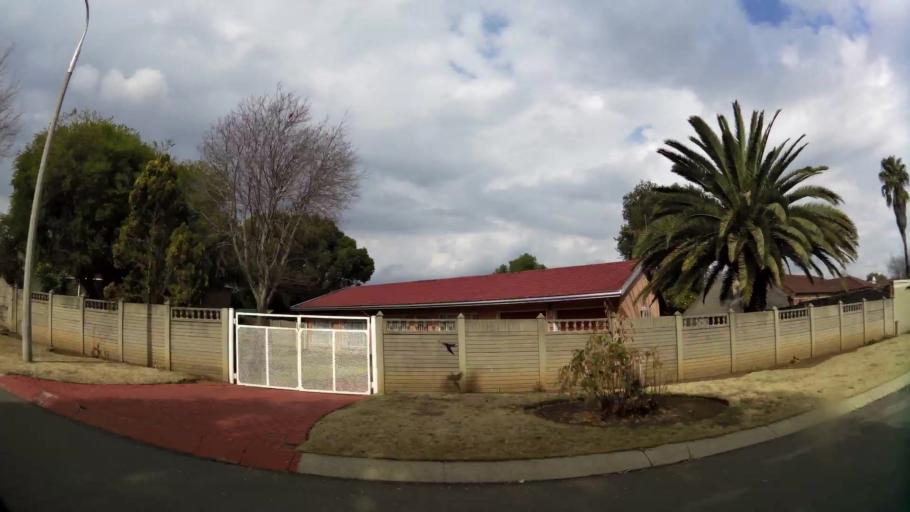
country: ZA
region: Gauteng
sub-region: Sedibeng District Municipality
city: Vanderbijlpark
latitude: -26.7085
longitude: 27.8024
